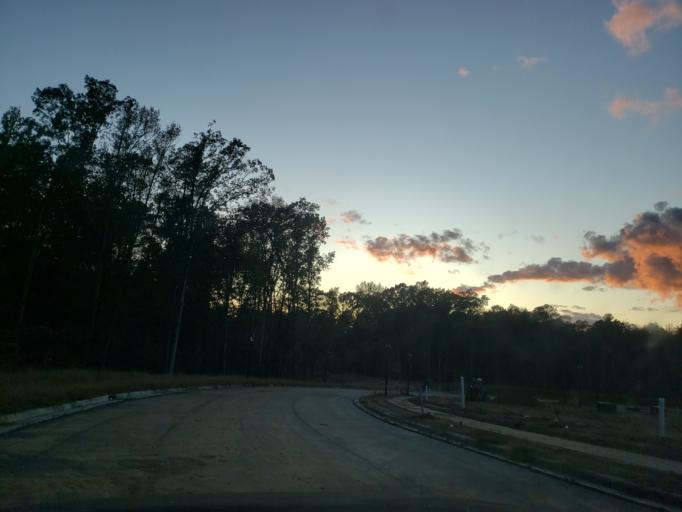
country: US
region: North Carolina
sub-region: Wake County
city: Green Level
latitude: 35.8763
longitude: -78.9536
